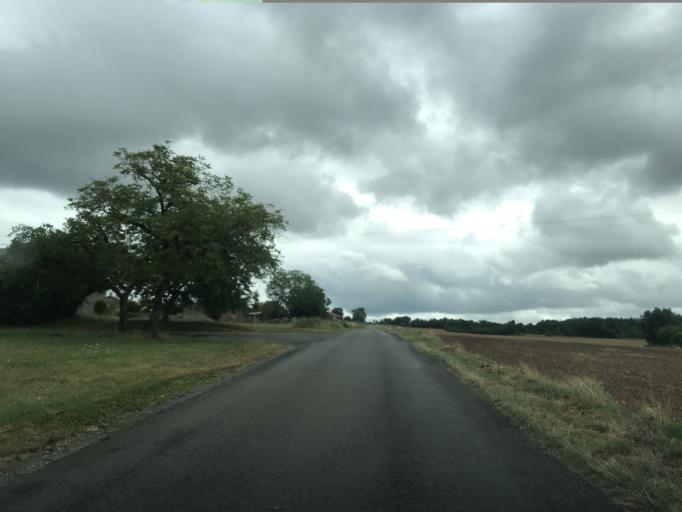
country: FR
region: Poitou-Charentes
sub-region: Departement de la Charente
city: Dirac
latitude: 45.5611
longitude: 0.2337
